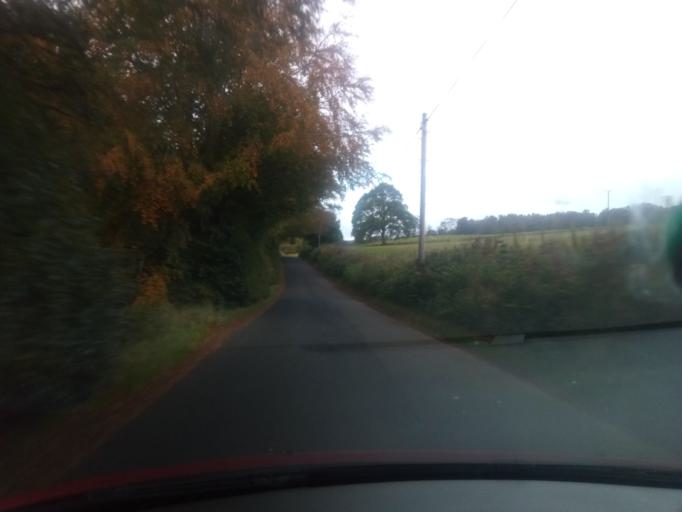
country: GB
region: Scotland
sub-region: The Scottish Borders
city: Jedburgh
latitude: 55.4526
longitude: -2.5661
